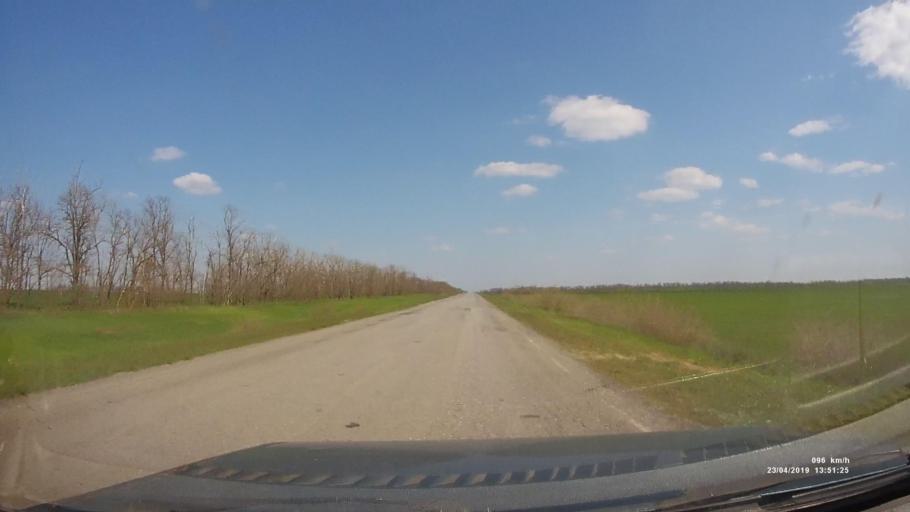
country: RU
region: Kalmykiya
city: Yashalta
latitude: 46.5994
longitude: 42.9349
